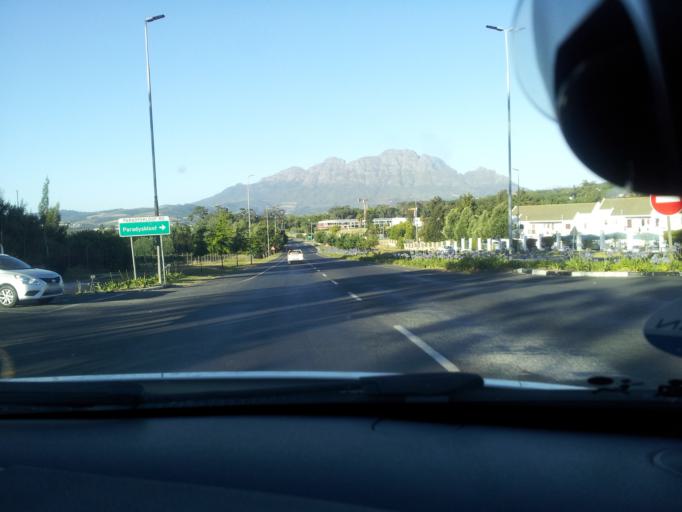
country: ZA
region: Western Cape
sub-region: Cape Winelands District Municipality
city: Stellenbosch
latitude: -33.9593
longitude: 18.8531
